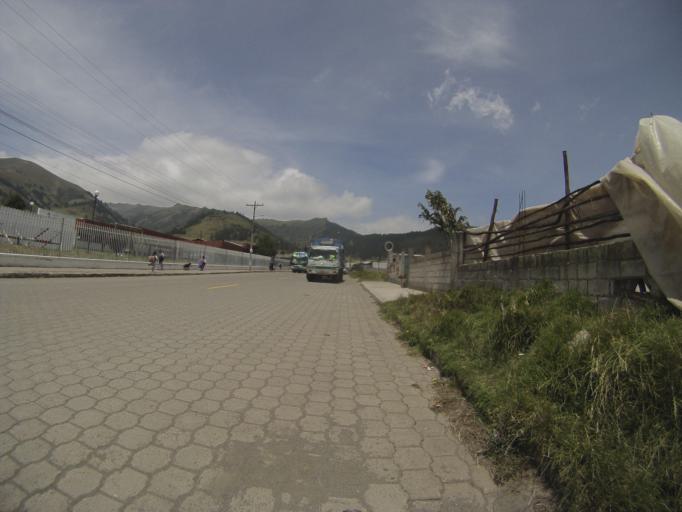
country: EC
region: Pichincha
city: Cayambe
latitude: 0.1571
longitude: -78.0694
